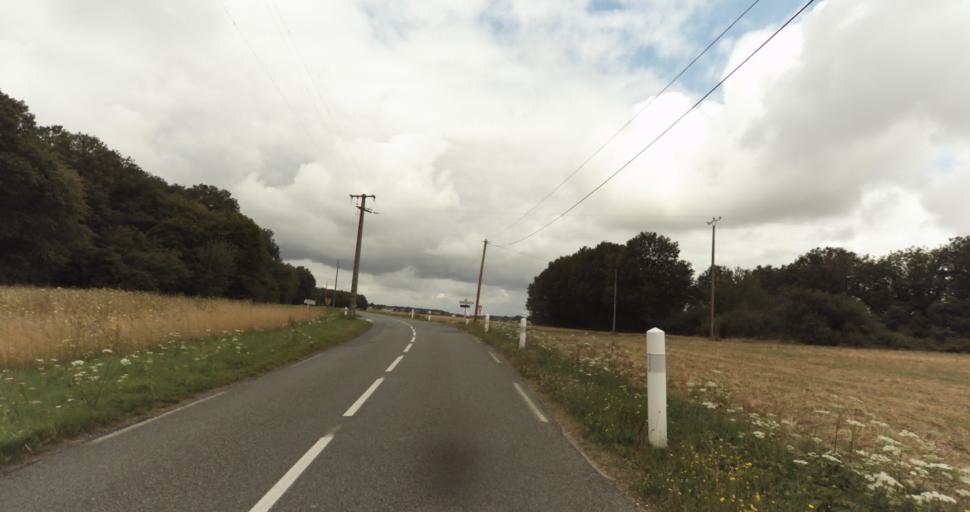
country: FR
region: Haute-Normandie
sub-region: Departement de l'Eure
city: Menilles
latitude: 48.9825
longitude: 1.2661
